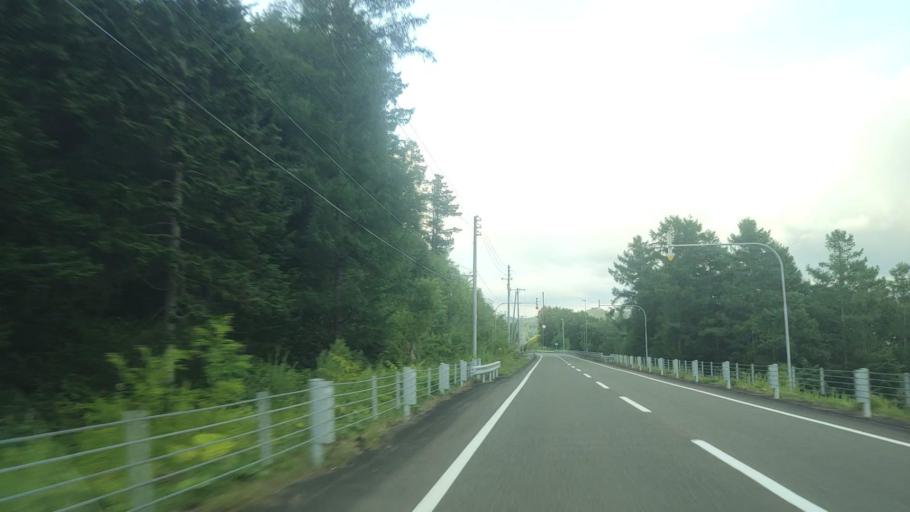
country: JP
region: Hokkaido
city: Bibai
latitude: 43.0665
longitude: 142.1022
